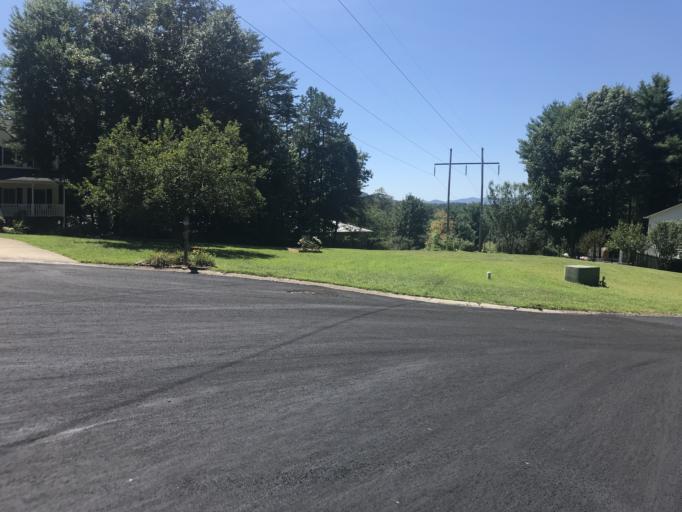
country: US
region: North Carolina
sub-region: Buncombe County
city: Biltmore Forest
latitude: 35.5484
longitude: -82.5044
